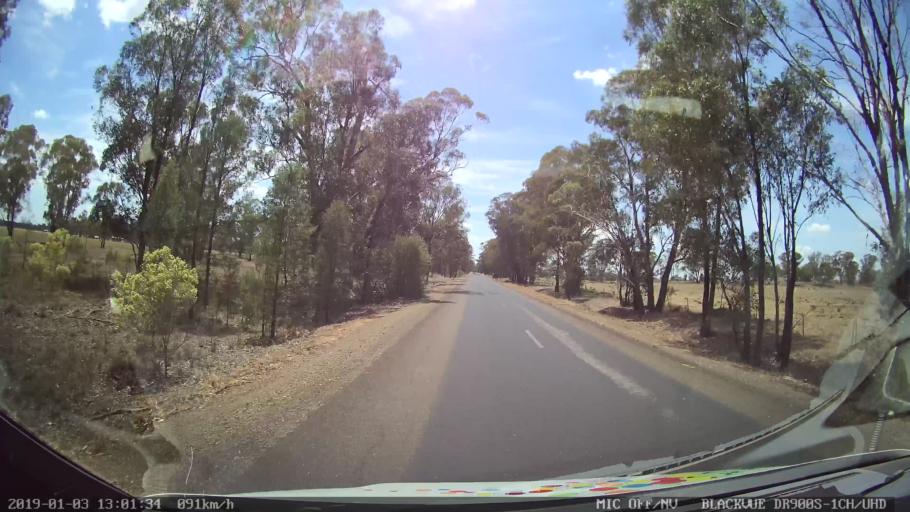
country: AU
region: New South Wales
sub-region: Cabonne
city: Canowindra
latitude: -33.6233
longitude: 148.4198
